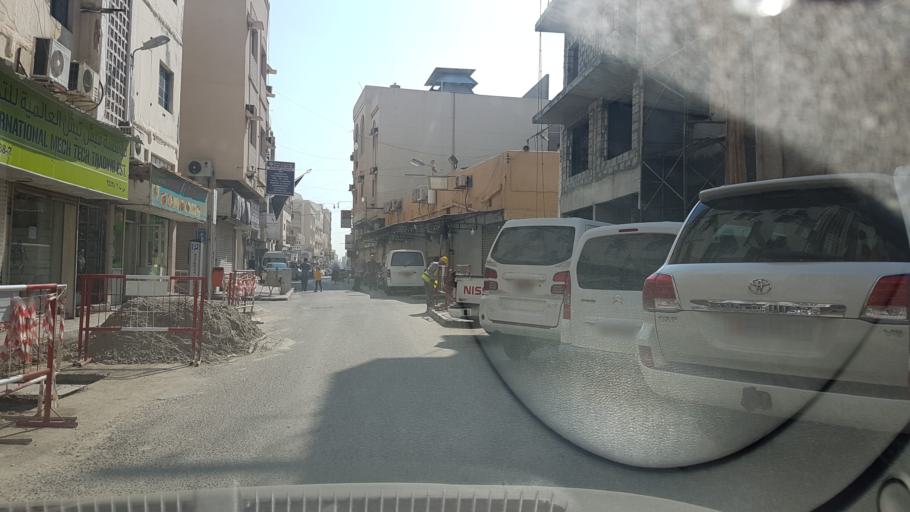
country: BH
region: Manama
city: Manama
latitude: 26.2332
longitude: 50.5803
